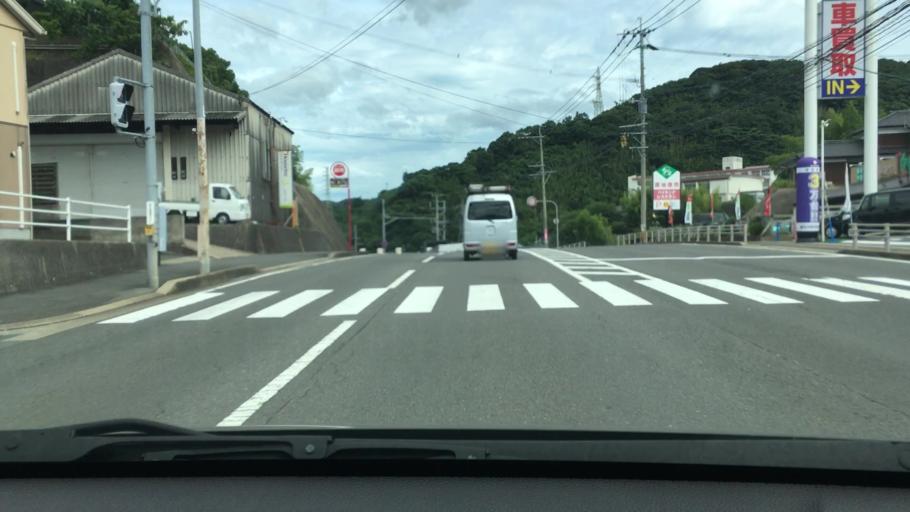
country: JP
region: Nagasaki
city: Togitsu
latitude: 32.8351
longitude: 129.8395
